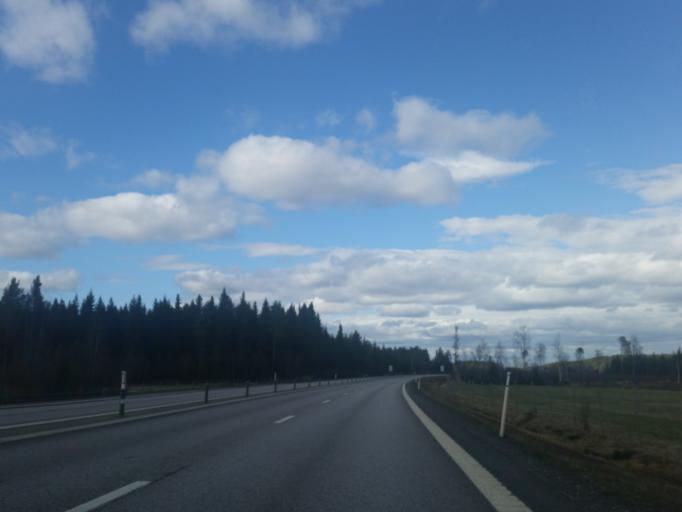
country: SE
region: Vaesterbotten
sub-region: Robertsfors Kommun
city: Robertsfors
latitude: 64.1207
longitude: 20.8824
